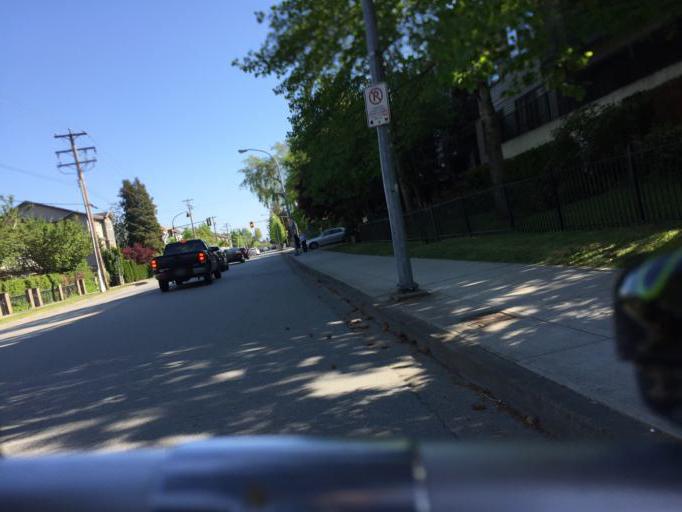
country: CA
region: British Columbia
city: Richmond
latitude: 49.1601
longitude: -123.1310
